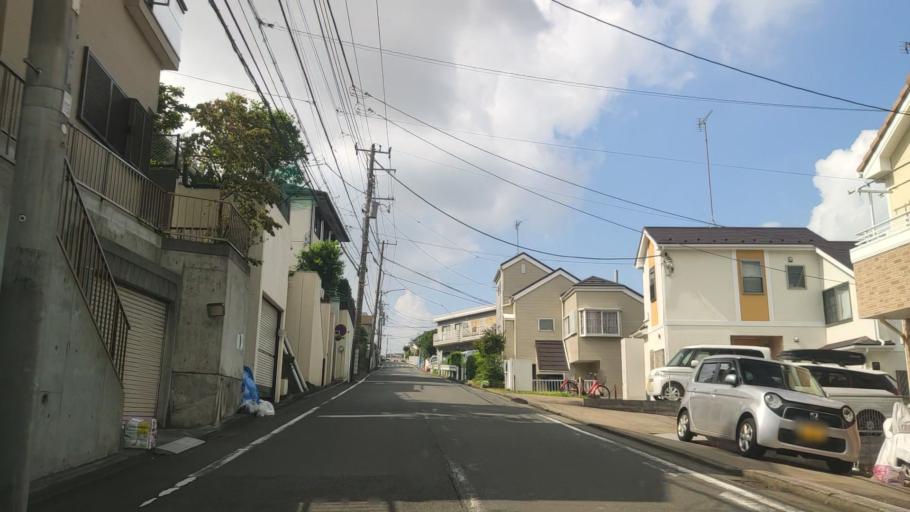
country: JP
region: Kanagawa
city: Yokohama
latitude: 35.4026
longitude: 139.5653
